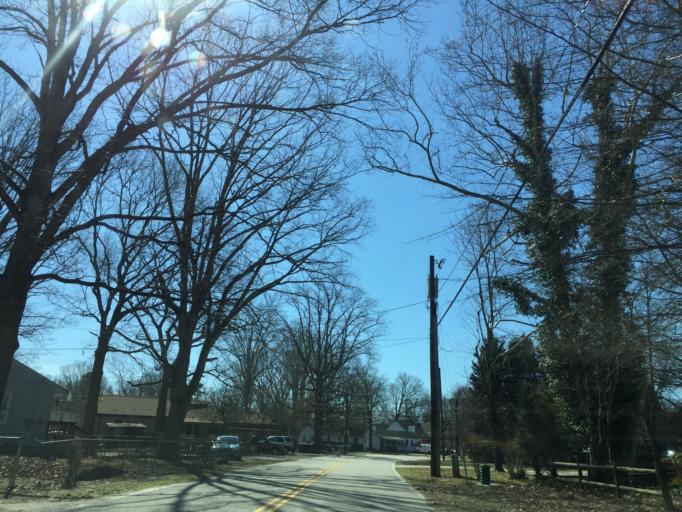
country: US
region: Virginia
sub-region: City of Newport News
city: Newport News
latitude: 37.0794
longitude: -76.5012
